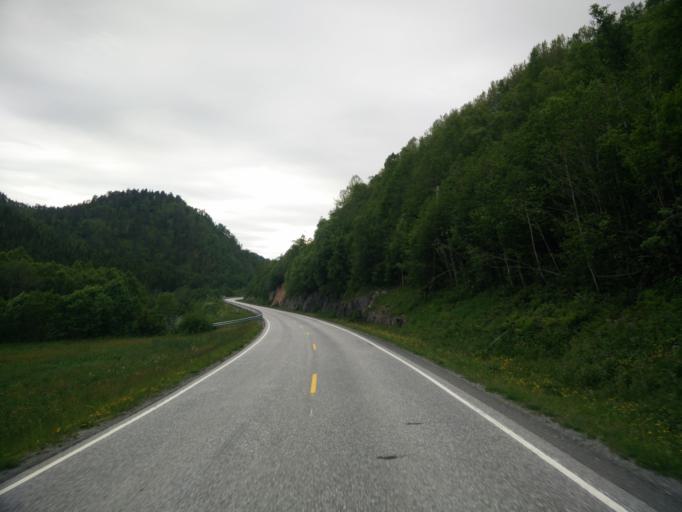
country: NO
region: Sor-Trondelag
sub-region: Hemne
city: Kyrksaeterora
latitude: 63.2103
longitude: 9.1548
